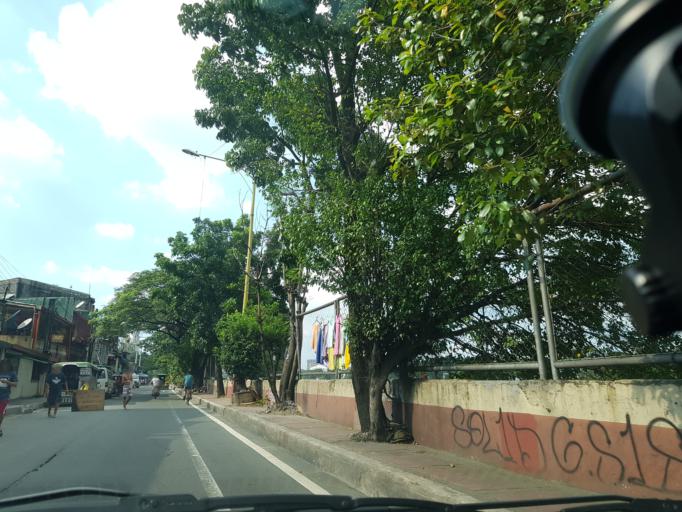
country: PH
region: Metro Manila
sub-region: Marikina
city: Calumpang
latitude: 14.5925
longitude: 121.0916
